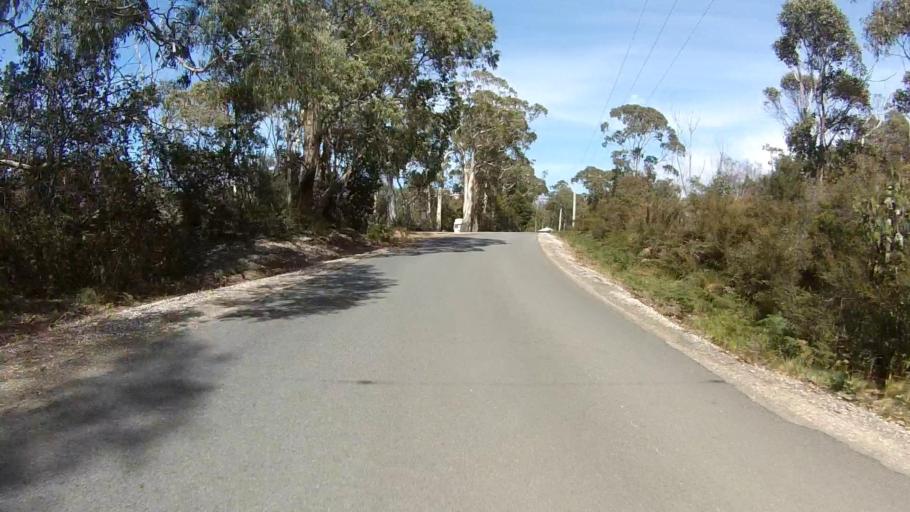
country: AU
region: Tasmania
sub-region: Huon Valley
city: Cygnet
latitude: -43.2425
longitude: 147.1219
